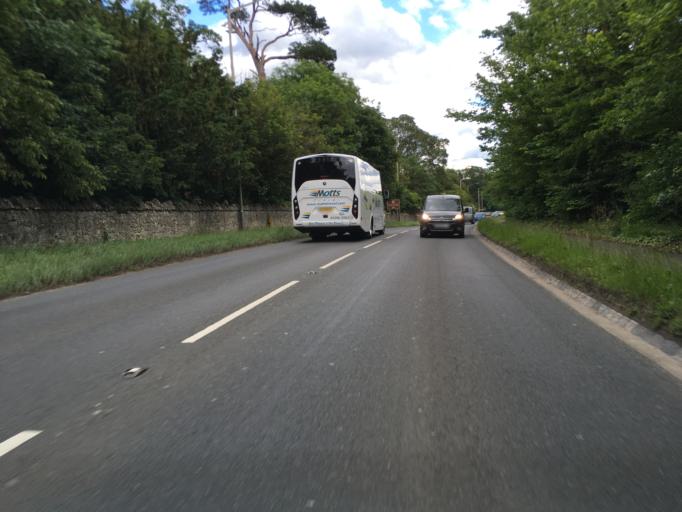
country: GB
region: England
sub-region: Buckinghamshire
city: Stone
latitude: 51.8037
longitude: -0.8530
